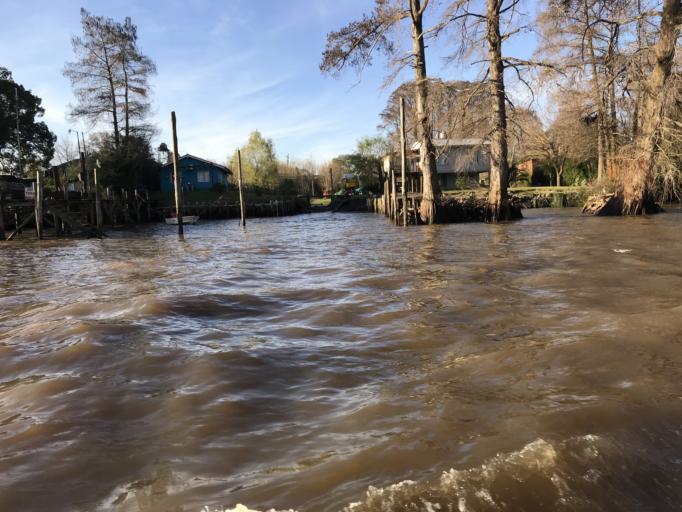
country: AR
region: Buenos Aires
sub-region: Partido de Tigre
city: Tigre
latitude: -34.4117
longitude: -58.5863
